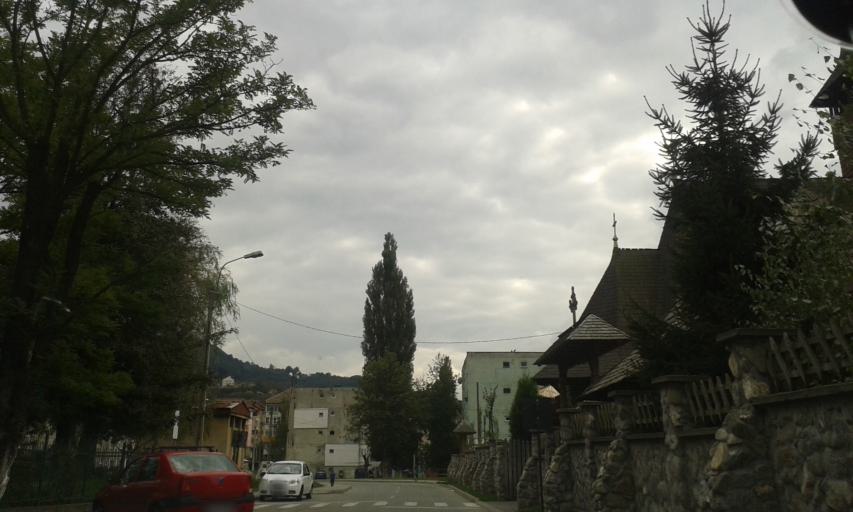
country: RO
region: Hunedoara
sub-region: Municipiul Petrosani
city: Petrosani
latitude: 45.3931
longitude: 23.3766
